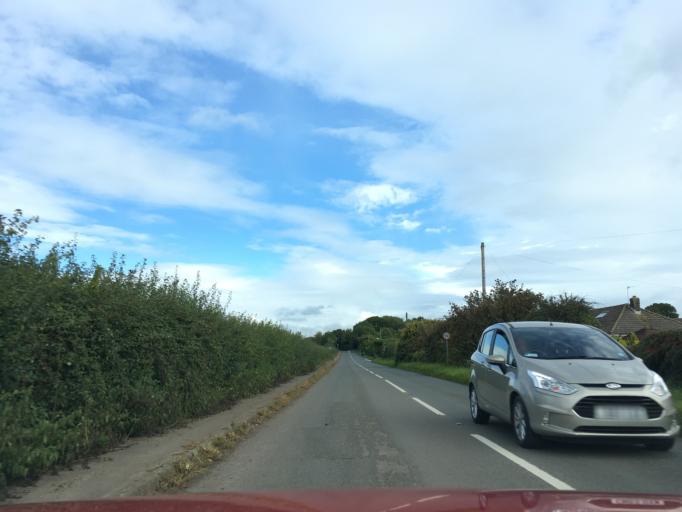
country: GB
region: Wales
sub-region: Monmouthshire
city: Chepstow
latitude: 51.6312
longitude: -2.6553
